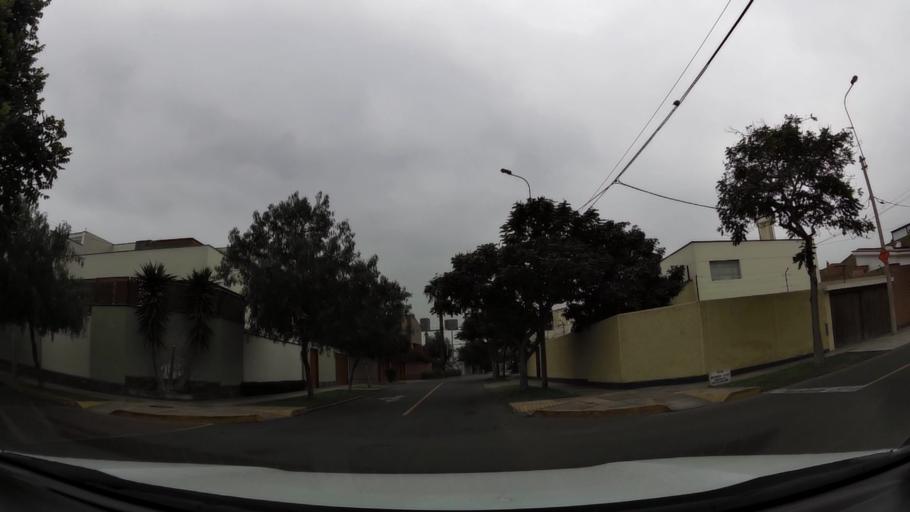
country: PE
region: Lima
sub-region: Lima
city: Surco
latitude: -12.1219
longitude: -77.0091
